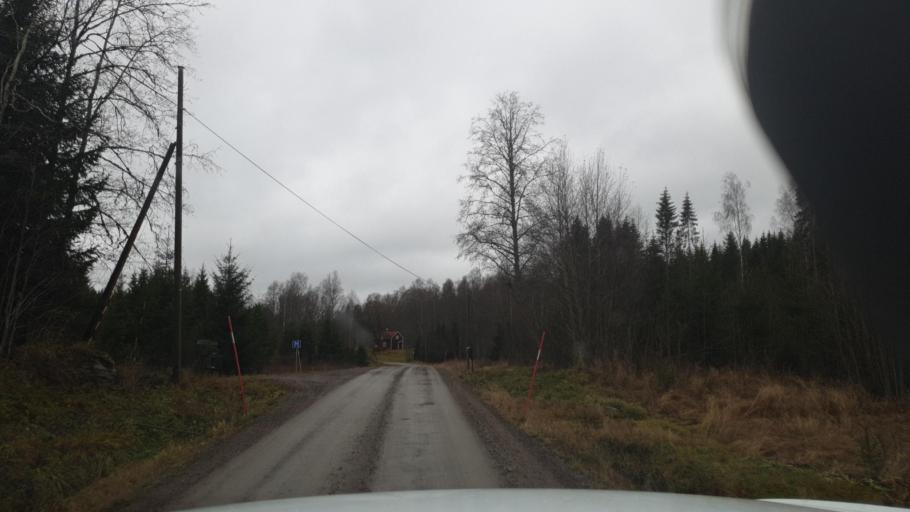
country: SE
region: Vaermland
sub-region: Eda Kommun
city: Charlottenberg
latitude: 59.9903
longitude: 12.4758
